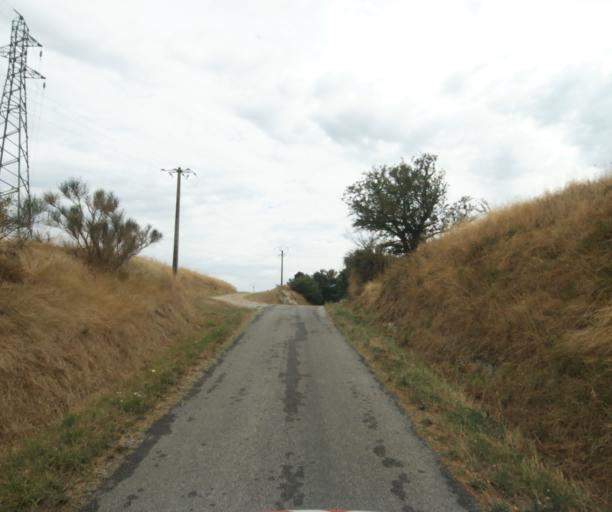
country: FR
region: Midi-Pyrenees
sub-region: Departement de la Haute-Garonne
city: Revel
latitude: 43.4301
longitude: 1.9661
